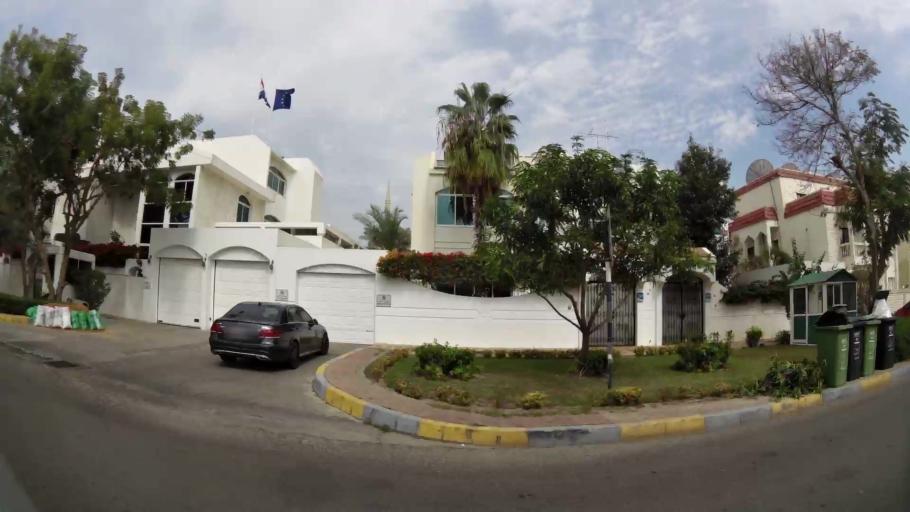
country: AE
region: Abu Dhabi
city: Abu Dhabi
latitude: 24.4571
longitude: 54.3659
